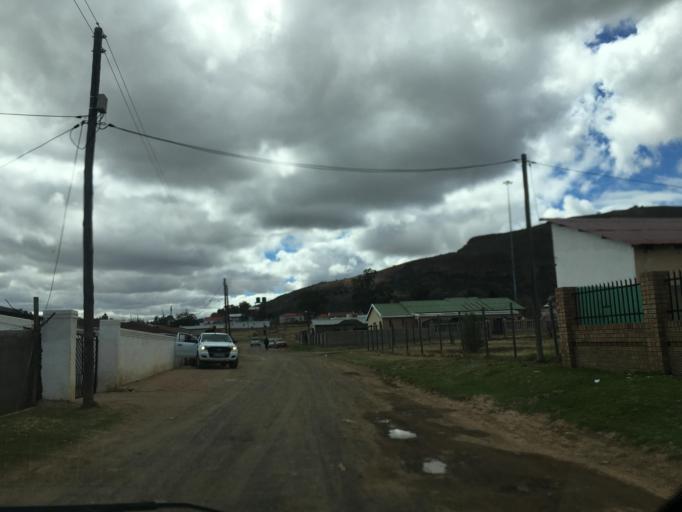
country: ZA
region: Eastern Cape
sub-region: Chris Hani District Municipality
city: Cala
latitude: -31.5303
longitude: 27.6972
